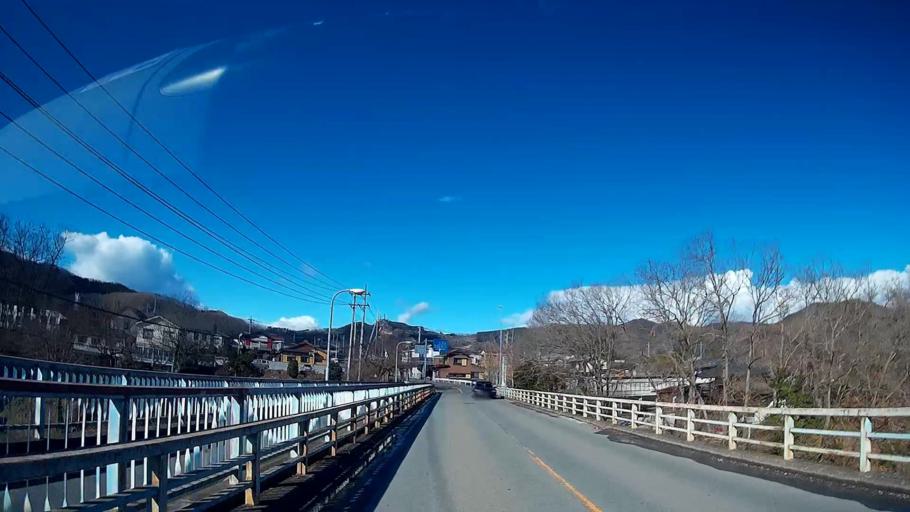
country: JP
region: Saitama
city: Kodamacho-kodamaminami
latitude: 36.1105
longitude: 139.1168
